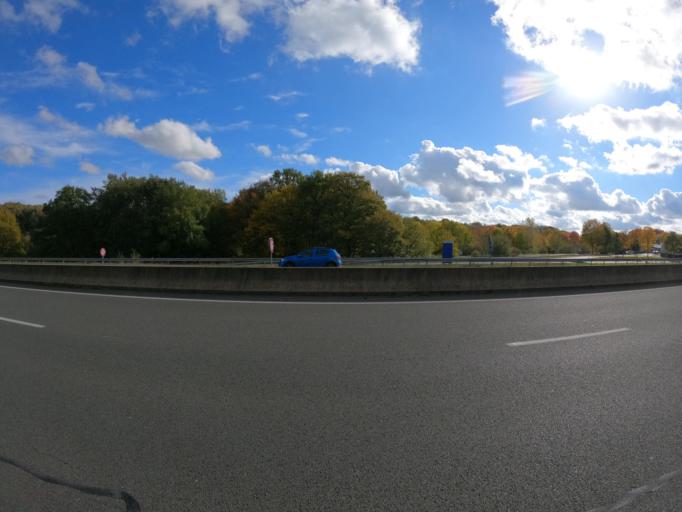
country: FR
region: Centre
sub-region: Departement d'Eure-et-Loir
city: Authon-du-Perche
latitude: 48.2138
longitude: 0.9421
